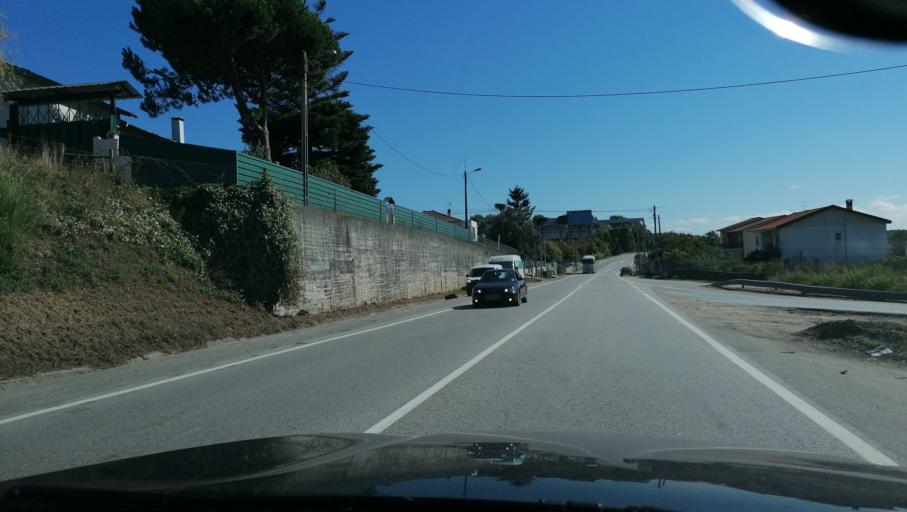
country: PT
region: Aveiro
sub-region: Estarreja
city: Salreu
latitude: 40.6891
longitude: -8.5565
